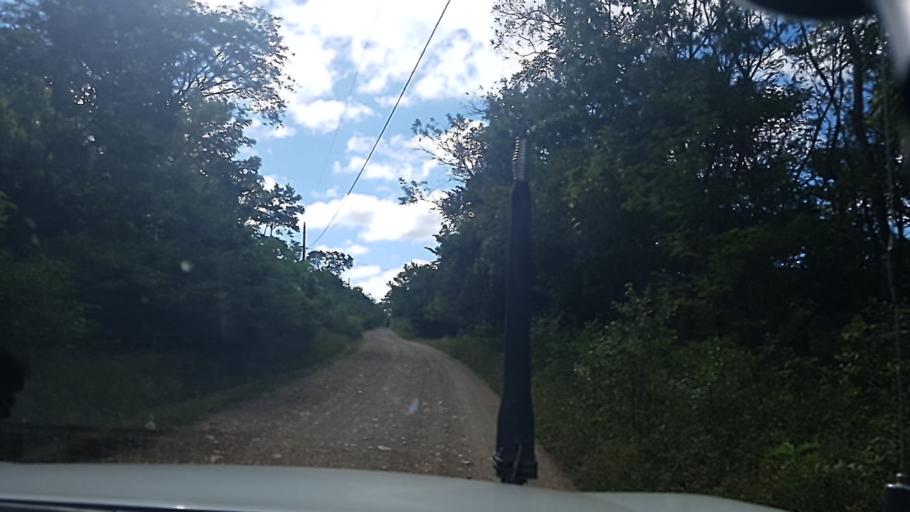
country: NI
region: Carazo
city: Santa Teresa
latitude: 11.6267
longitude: -86.1652
